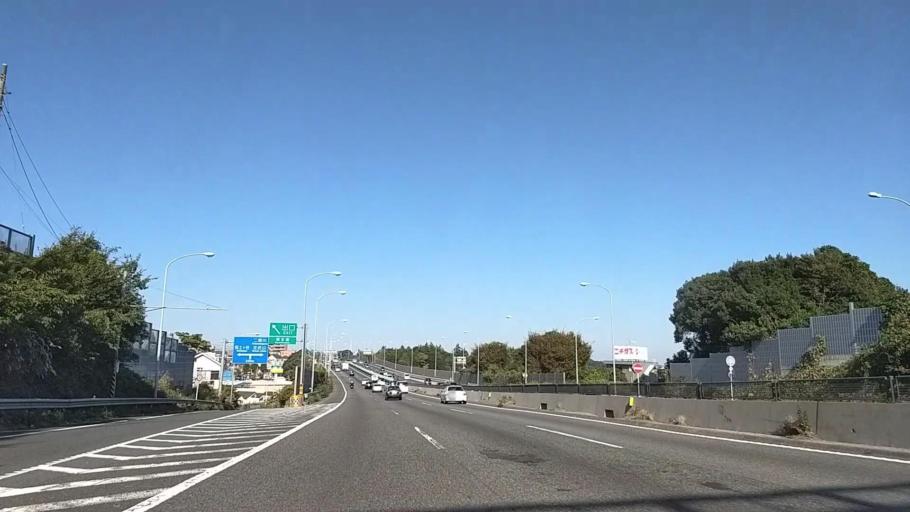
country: JP
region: Kanagawa
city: Minami-rinkan
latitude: 35.4608
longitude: 139.5441
